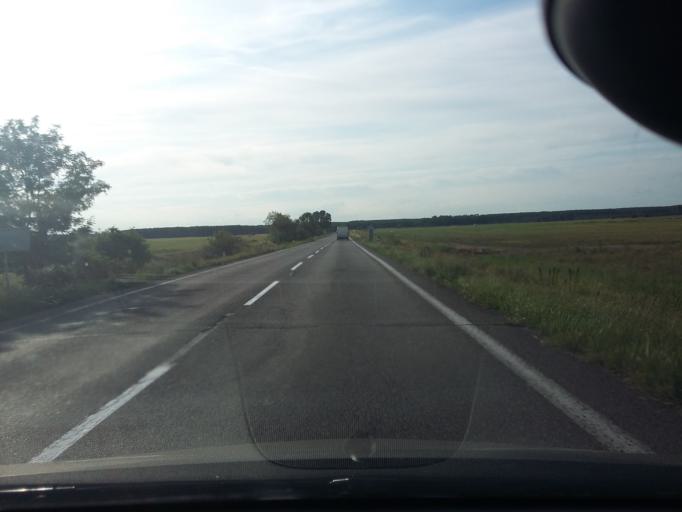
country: SK
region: Bratislavsky
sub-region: Okres Malacky
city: Malacky
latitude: 48.3802
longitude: 17.1187
